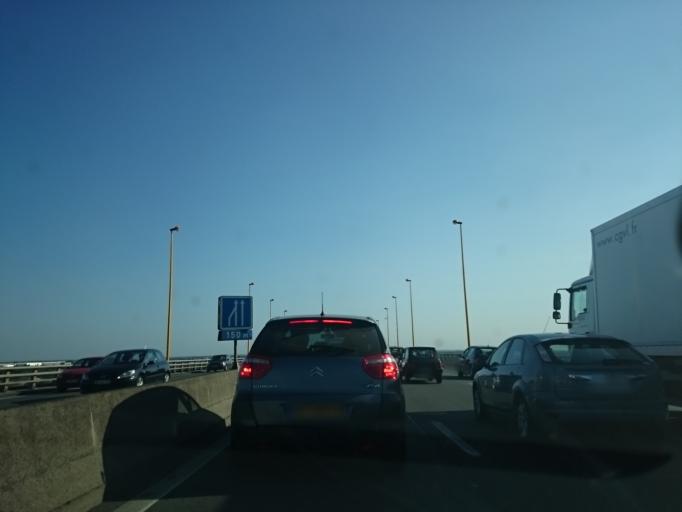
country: FR
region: Pays de la Loire
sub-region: Departement de la Loire-Atlantique
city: Bouguenais
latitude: 47.1930
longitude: -1.6136
